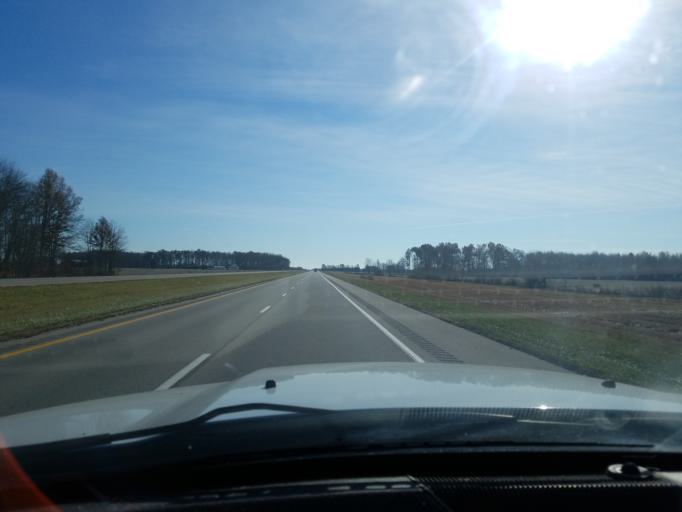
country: US
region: Ohio
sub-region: Adams County
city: Winchester
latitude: 38.9984
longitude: -83.7744
